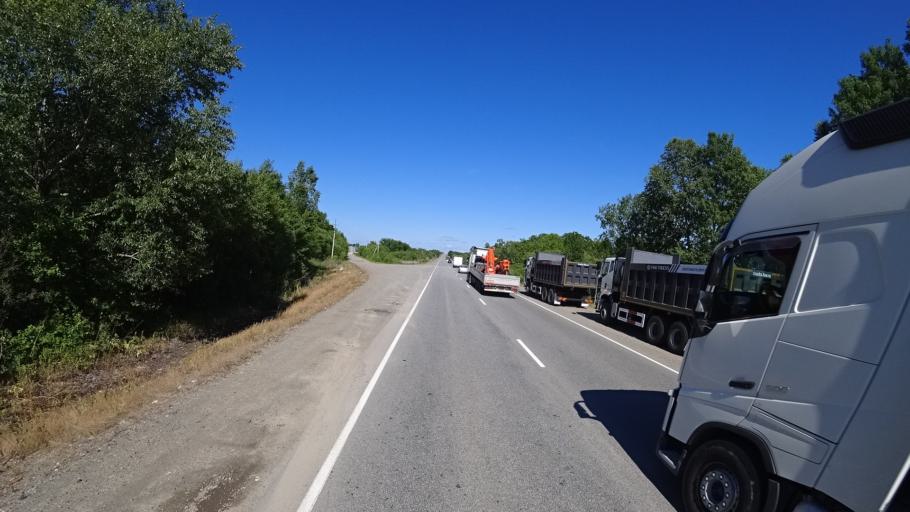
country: RU
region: Khabarovsk Krai
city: Khor
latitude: 47.8924
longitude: 135.0028
